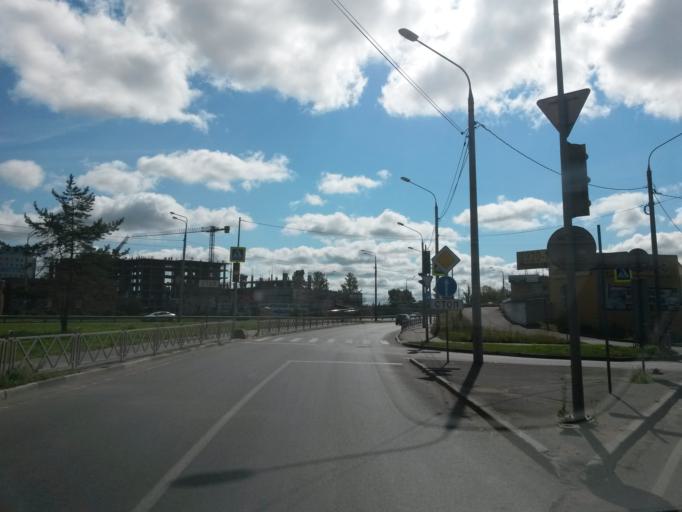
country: RU
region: Jaroslavl
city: Yaroslavl
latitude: 57.6179
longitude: 39.8576
